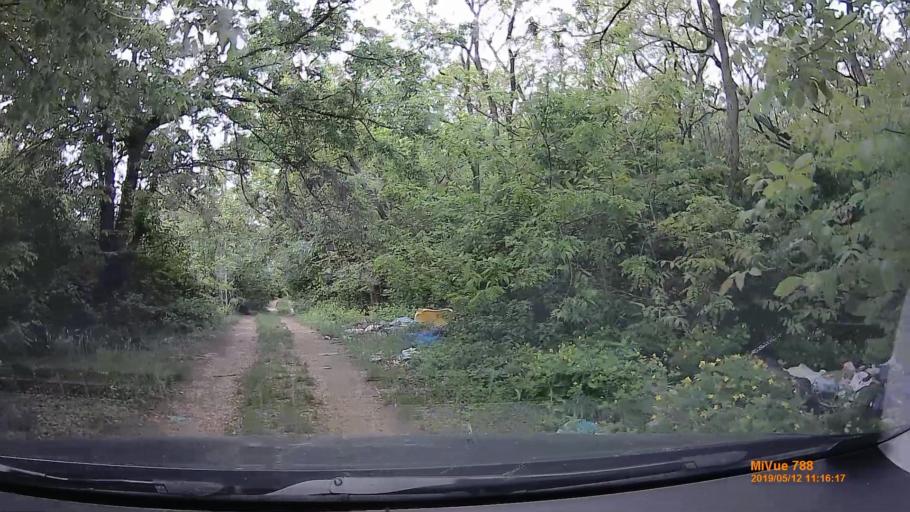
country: HU
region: Budapest
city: Budapest XVII. keruelet
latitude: 47.4658
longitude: 19.2290
